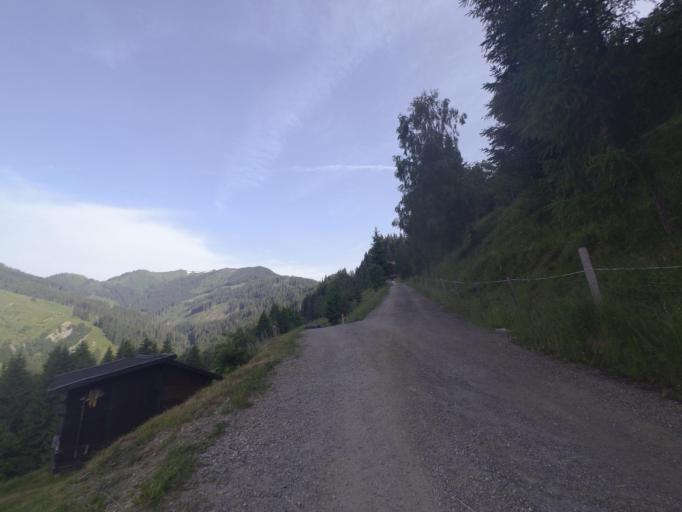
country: AT
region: Salzburg
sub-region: Politischer Bezirk Sankt Johann im Pongau
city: Muhlbach am Hochkonig
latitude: 47.3574
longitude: 13.1150
